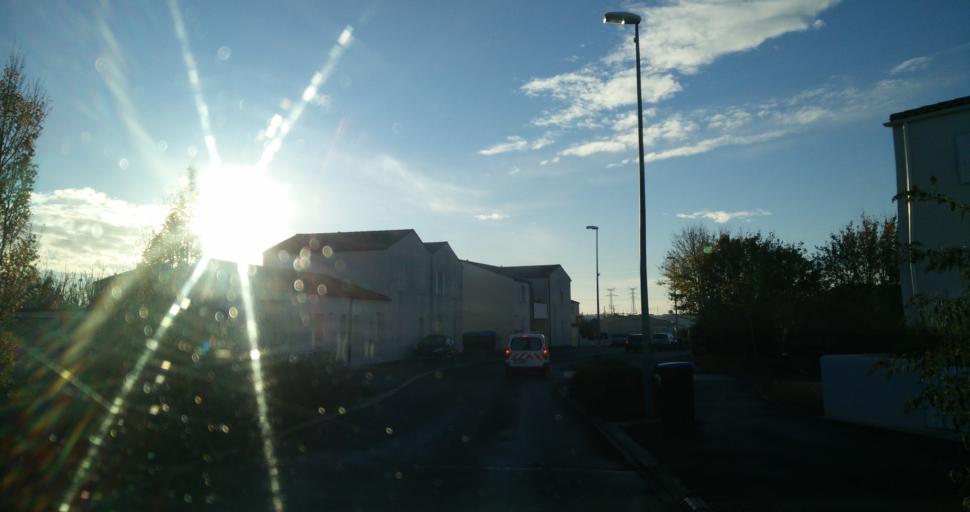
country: FR
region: Poitou-Charentes
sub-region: Departement de la Charente-Maritime
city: Puilboreau
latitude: 46.1832
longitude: -1.1257
